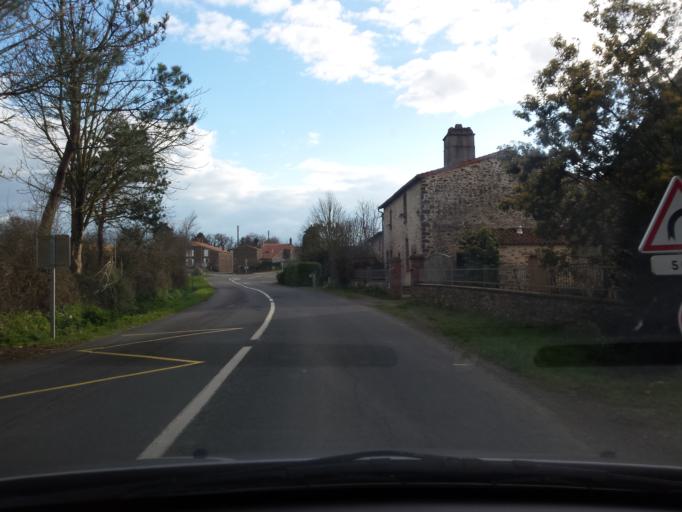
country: FR
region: Pays de la Loire
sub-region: Departement de la Vendee
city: Saint-Martin-des-Noyers
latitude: 46.7147
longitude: -1.2108
